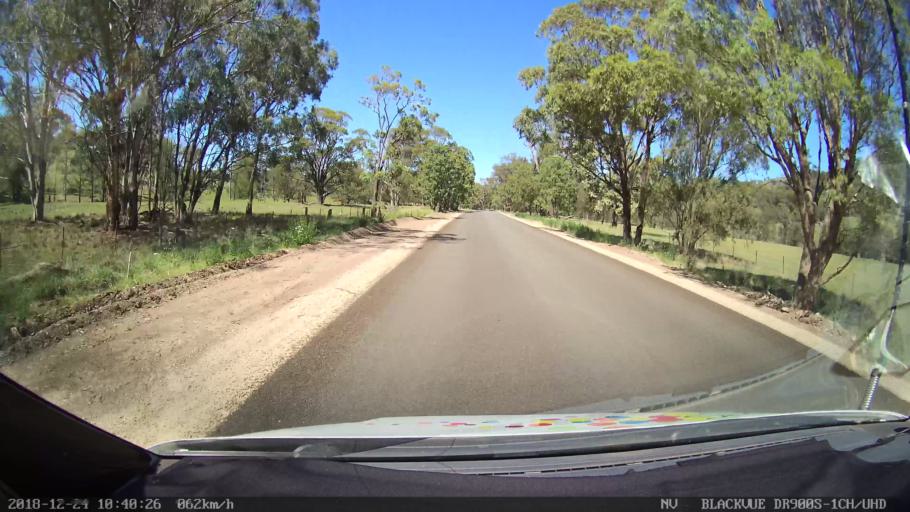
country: AU
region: New South Wales
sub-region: Upper Hunter Shire
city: Merriwa
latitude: -31.8617
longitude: 150.4673
